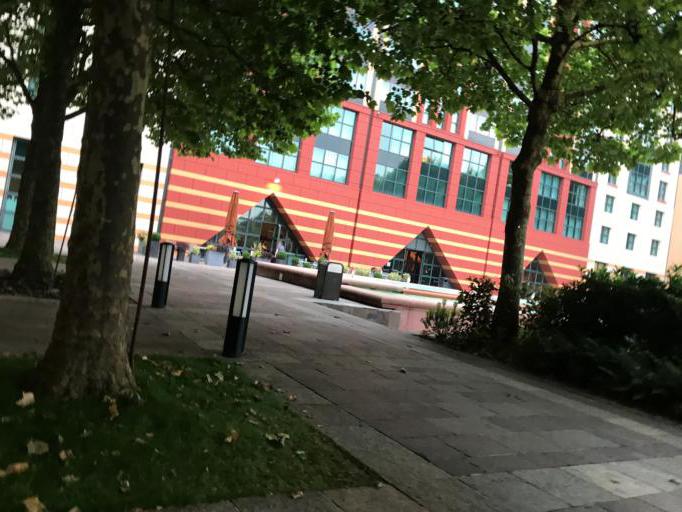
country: FR
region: Ile-de-France
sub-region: Departement de Seine-et-Marne
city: Chalifert
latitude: 48.8701
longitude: 2.7875
